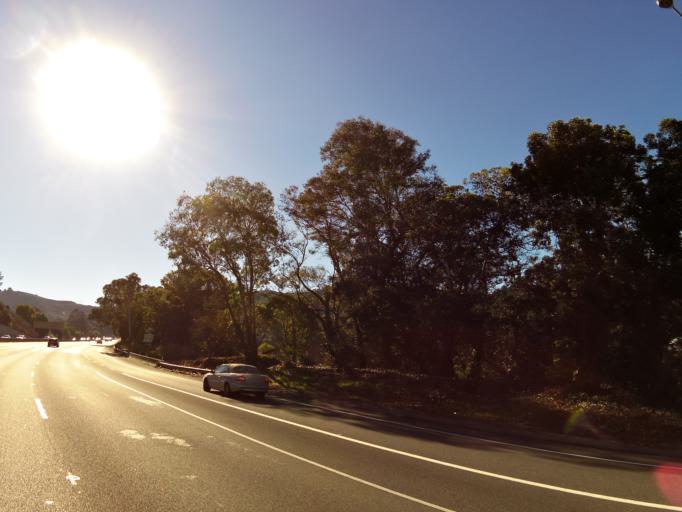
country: US
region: California
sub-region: Marin County
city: Marin City
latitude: 37.8724
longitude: -122.5075
